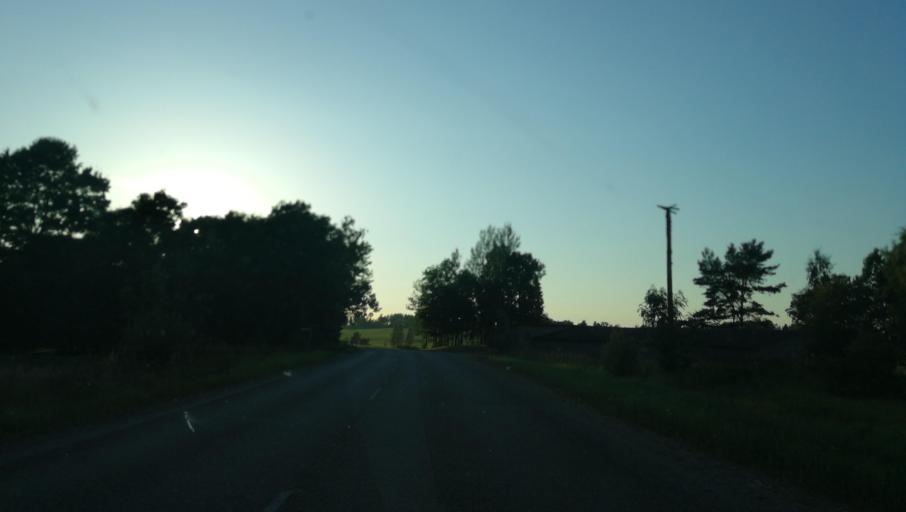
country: LV
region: Priekuli
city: Priekuli
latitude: 57.2644
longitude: 25.3540
